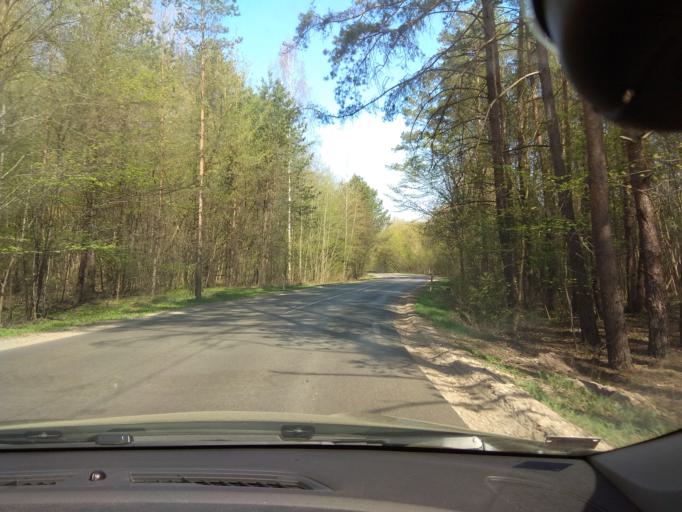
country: LT
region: Vilnius County
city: Lazdynai
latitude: 54.6555
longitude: 25.1801
